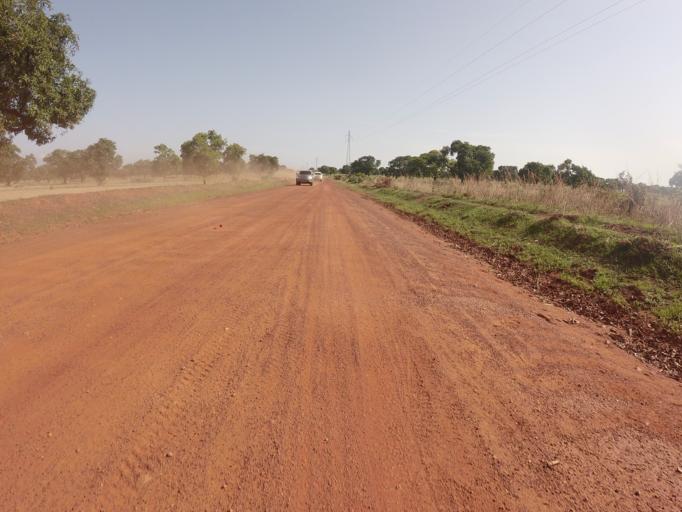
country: GH
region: Upper East
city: Bawku
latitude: 10.7773
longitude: -0.1926
